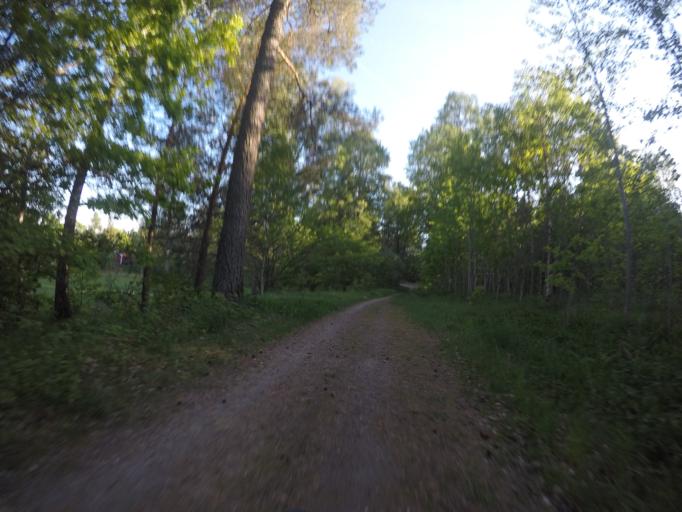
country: SE
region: Soedermanland
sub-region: Eskilstuna Kommun
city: Eskilstuna
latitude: 59.3407
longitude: 16.5270
